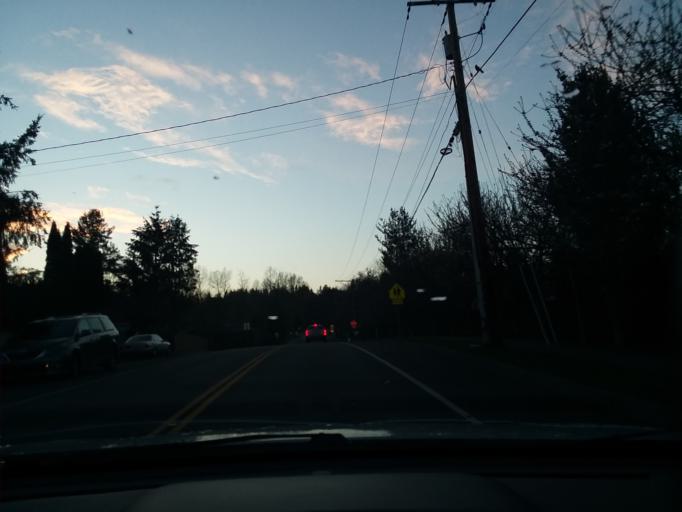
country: US
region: Washington
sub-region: King County
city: Kenmore
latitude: 47.7781
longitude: -122.2518
